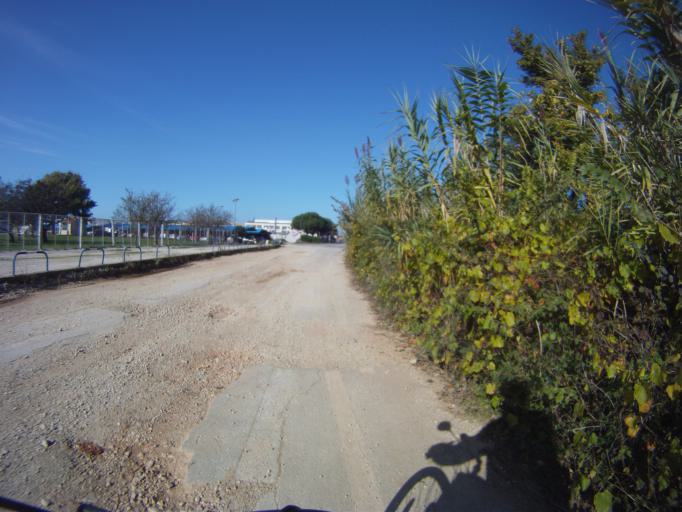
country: HR
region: Istarska
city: Umag
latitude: 45.4205
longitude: 13.5300
